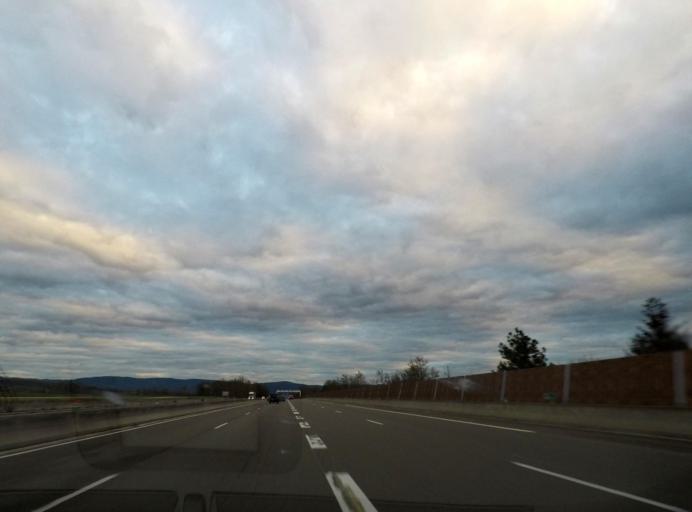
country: FR
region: Rhone-Alpes
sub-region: Departement de l'Ain
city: Saint-Martin-du-Mont
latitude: 46.0762
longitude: 5.3047
